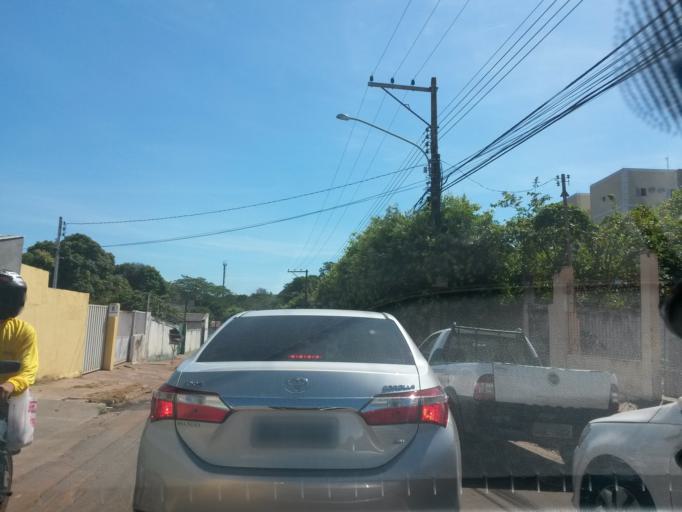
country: BR
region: Mato Grosso
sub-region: Cuiaba
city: Cuiaba
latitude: -15.6259
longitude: -56.0580
